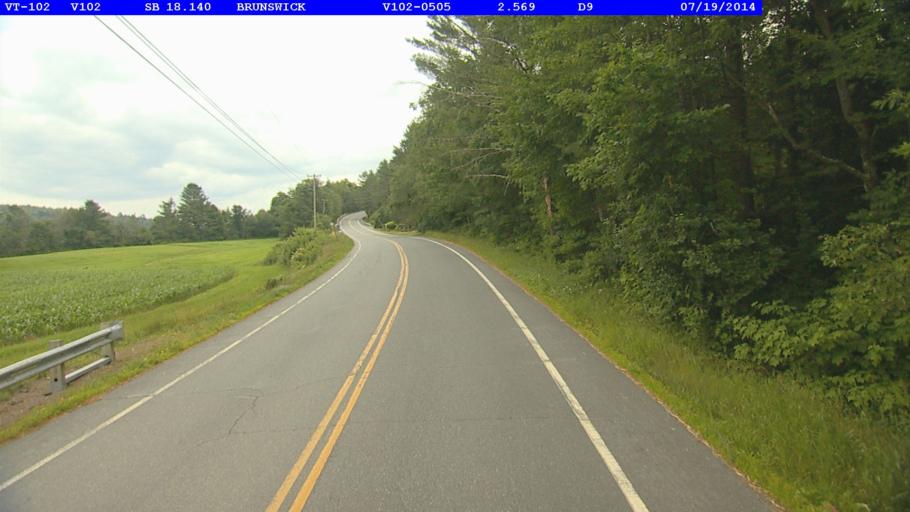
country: US
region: New Hampshire
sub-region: Coos County
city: Stratford
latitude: 44.6961
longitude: -71.6028
